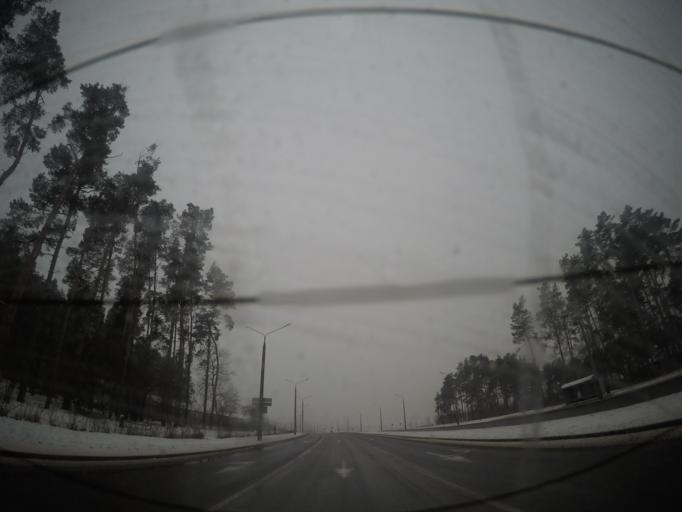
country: BY
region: Grodnenskaya
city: Hrodna
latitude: 53.6328
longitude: 23.8070
